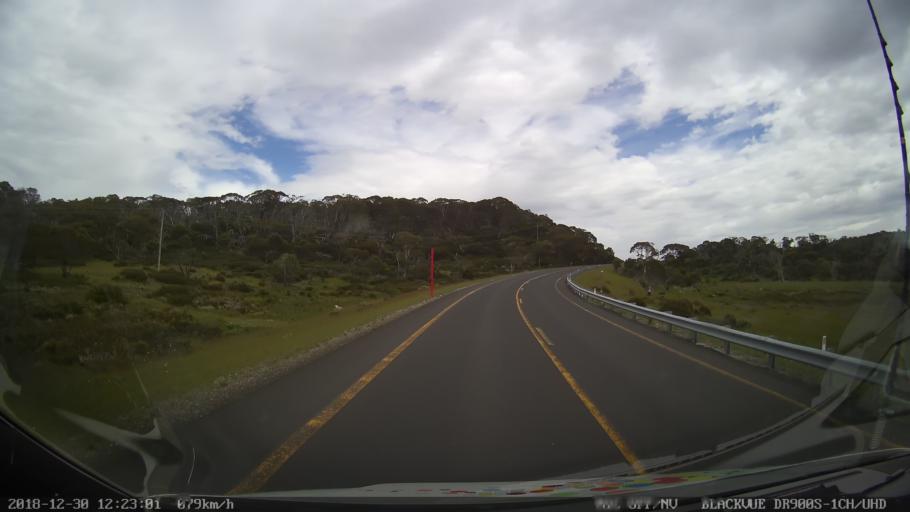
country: AU
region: New South Wales
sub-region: Snowy River
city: Jindabyne
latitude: -36.3626
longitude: 148.5042
